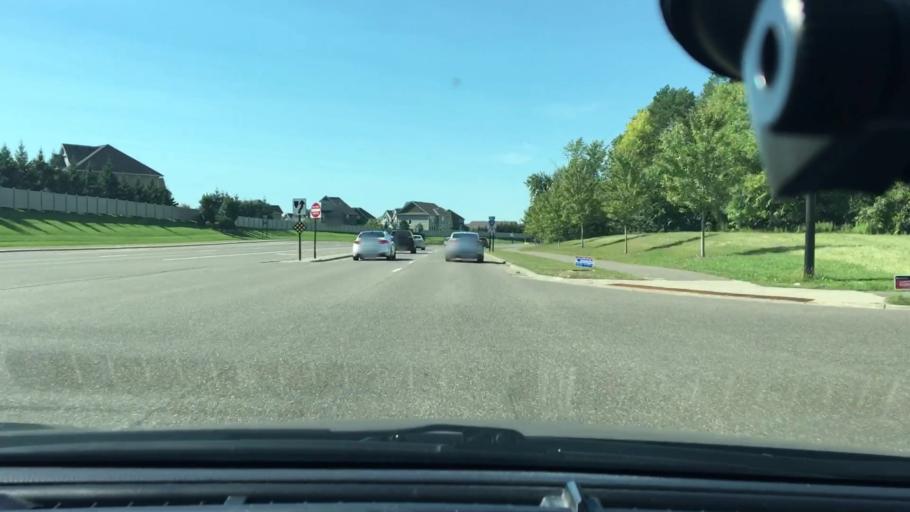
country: US
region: Minnesota
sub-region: Hennepin County
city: Maple Grove
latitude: 45.0837
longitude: -93.4980
